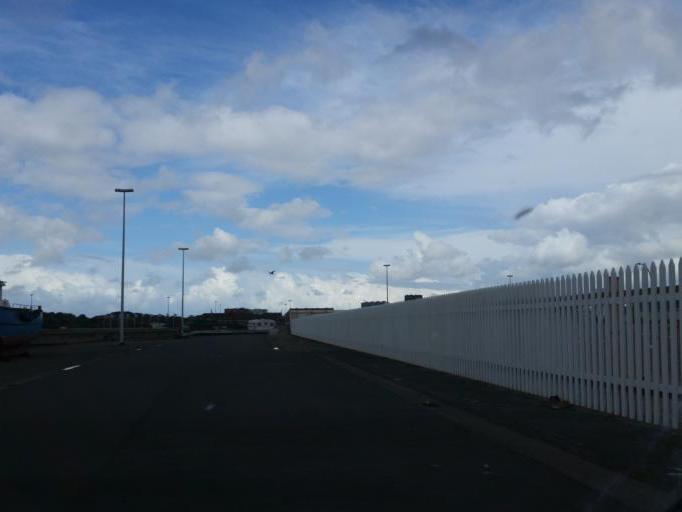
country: BE
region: Flanders
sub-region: Provincie West-Vlaanderen
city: Ostend
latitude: 51.2359
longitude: 2.9316
